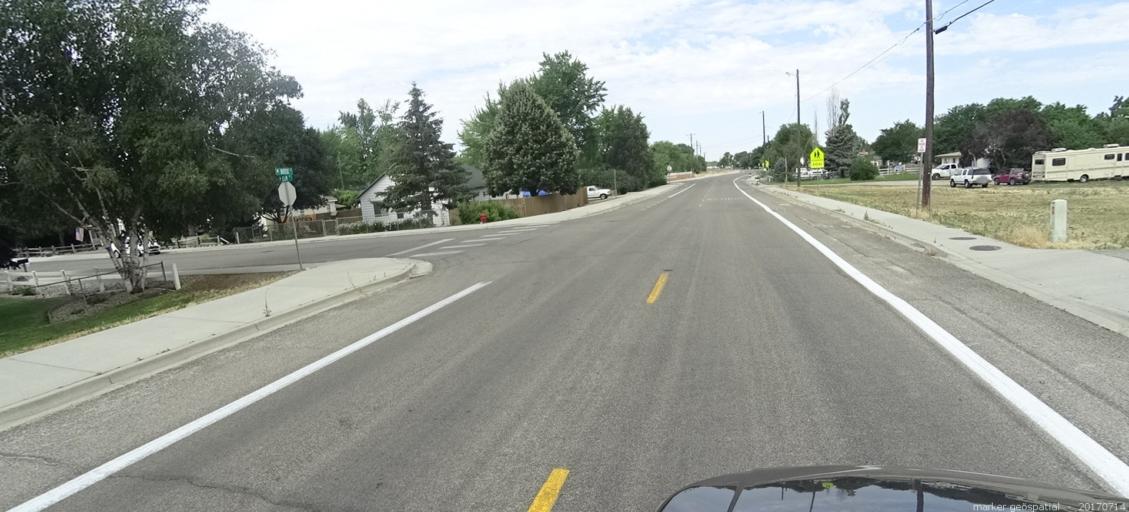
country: US
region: Idaho
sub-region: Ada County
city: Kuna
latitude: 43.4958
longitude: -116.4171
